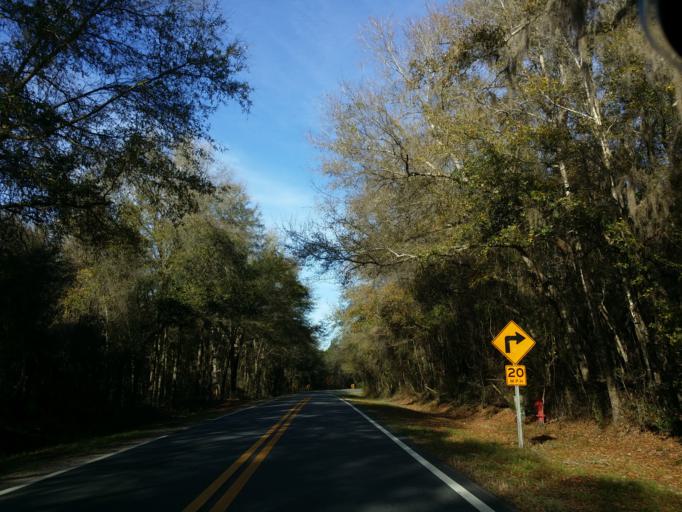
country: US
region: Florida
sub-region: Leon County
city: Woodville
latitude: 30.3794
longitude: -84.1535
